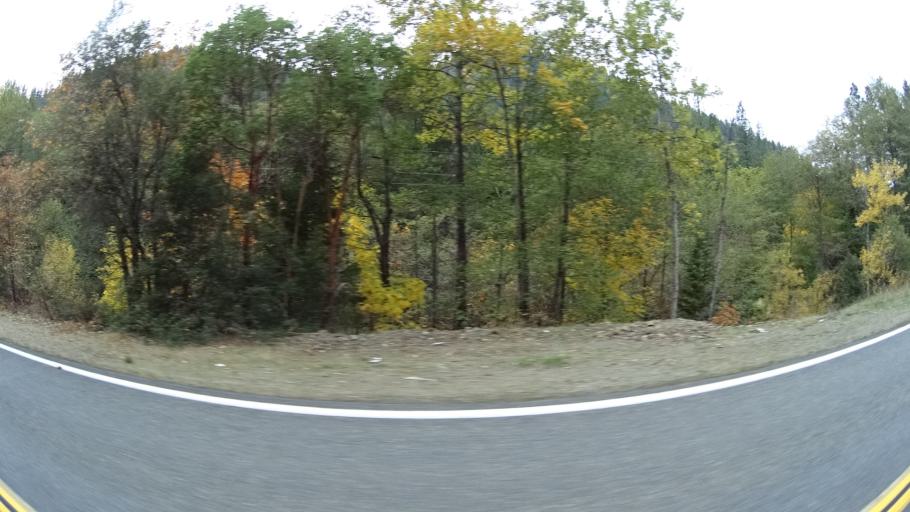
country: US
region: California
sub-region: Siskiyou County
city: Happy Camp
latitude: 41.8885
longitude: -123.4331
